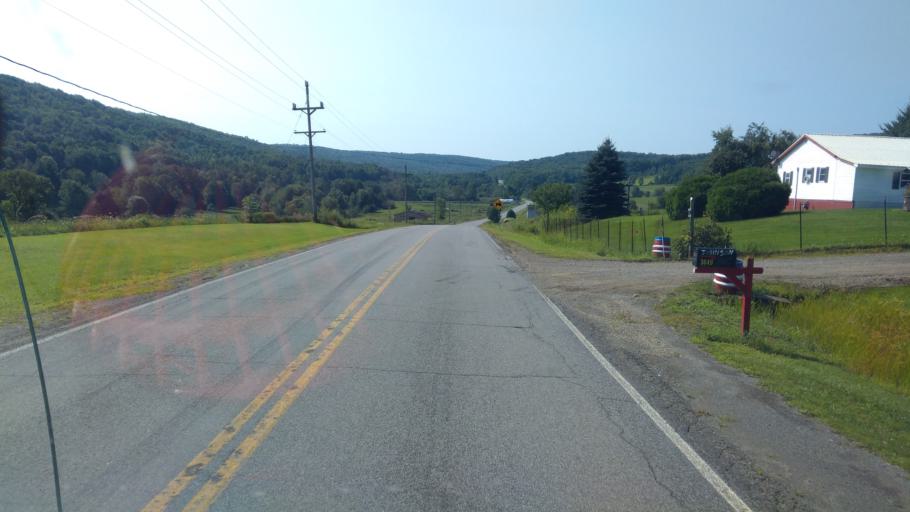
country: US
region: New York
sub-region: Allegany County
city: Friendship
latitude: 42.1580
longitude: -78.1482
